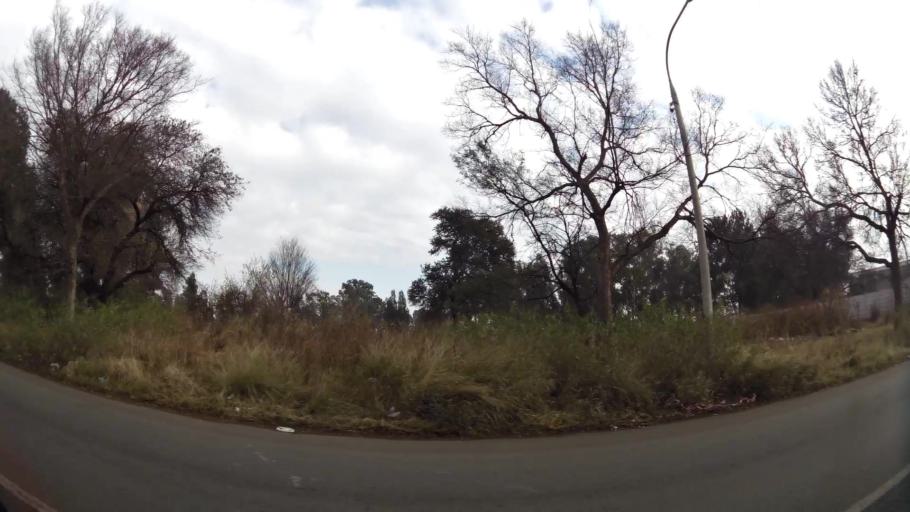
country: ZA
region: Gauteng
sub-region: Sedibeng District Municipality
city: Vanderbijlpark
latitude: -26.6932
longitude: 27.8120
